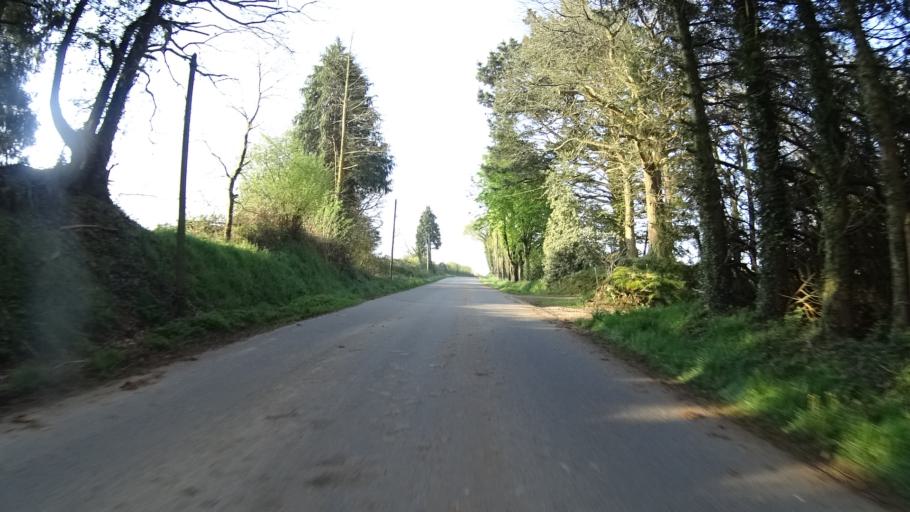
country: FR
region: Brittany
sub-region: Departement du Finistere
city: Sizun
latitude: 48.4319
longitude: -4.0717
